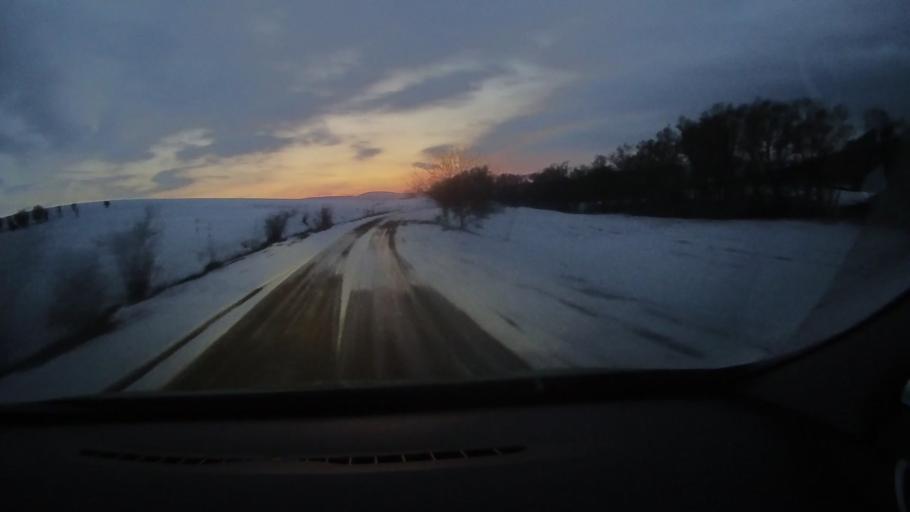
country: RO
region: Harghita
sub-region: Comuna Darjiu
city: Darjiu
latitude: 46.1656
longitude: 25.2189
